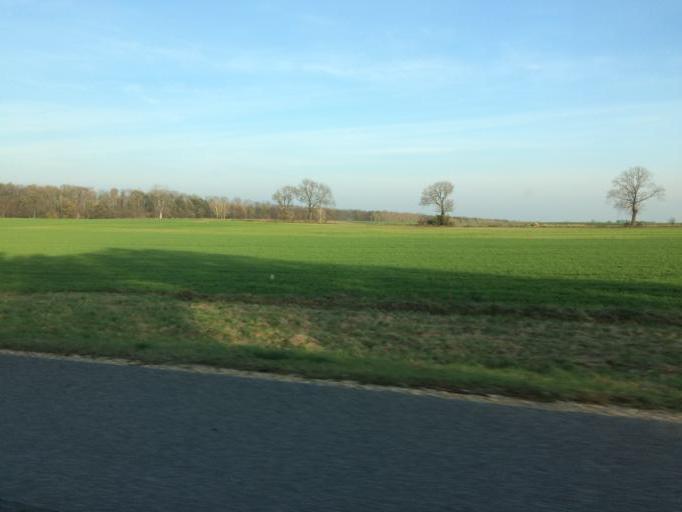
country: PL
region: Opole Voivodeship
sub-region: Powiat strzelecki
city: Strzelce Opolskie
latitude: 50.4989
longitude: 18.3380
